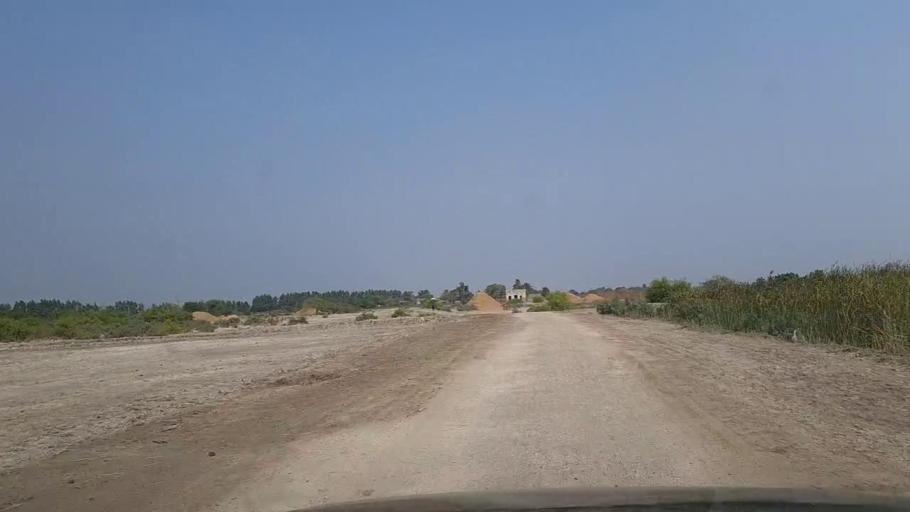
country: PK
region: Sindh
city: Thatta
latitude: 24.7507
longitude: 67.7981
